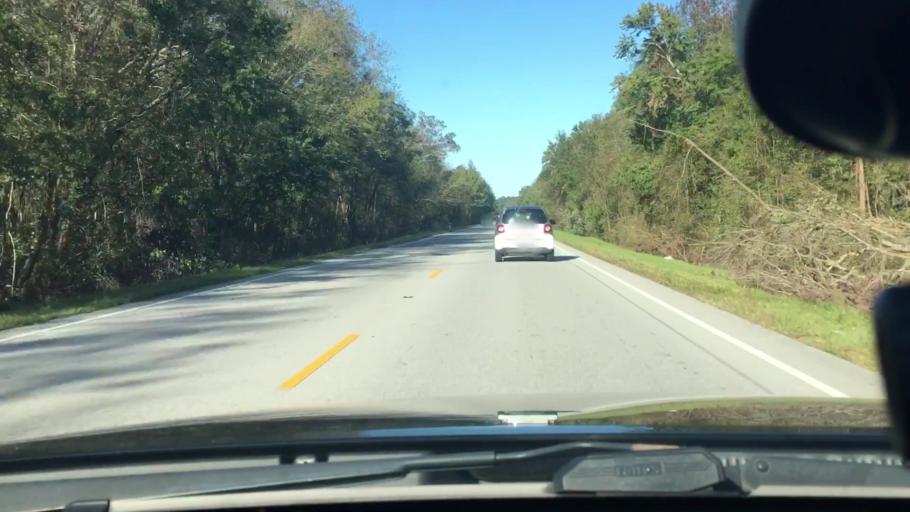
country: US
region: North Carolina
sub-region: Craven County
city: Vanceboro
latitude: 35.2061
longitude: -77.1259
